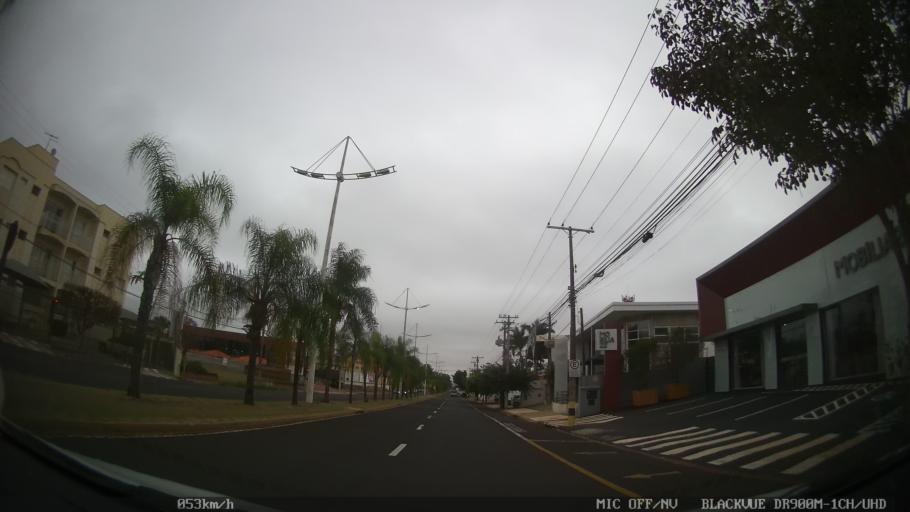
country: BR
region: Sao Paulo
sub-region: Sao Jose Do Rio Preto
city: Sao Jose do Rio Preto
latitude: -20.8414
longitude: -49.4019
